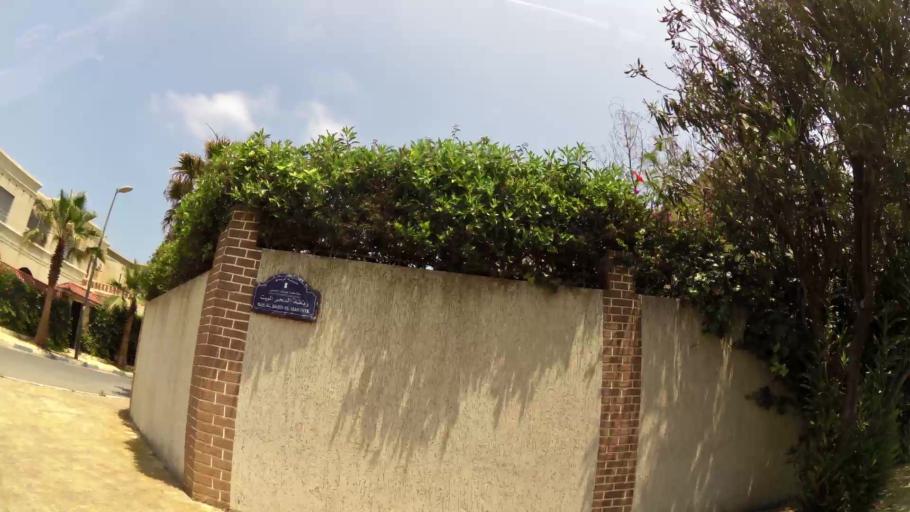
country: MA
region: Rabat-Sale-Zemmour-Zaer
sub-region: Skhirate-Temara
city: Temara
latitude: 33.9689
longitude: -6.9066
